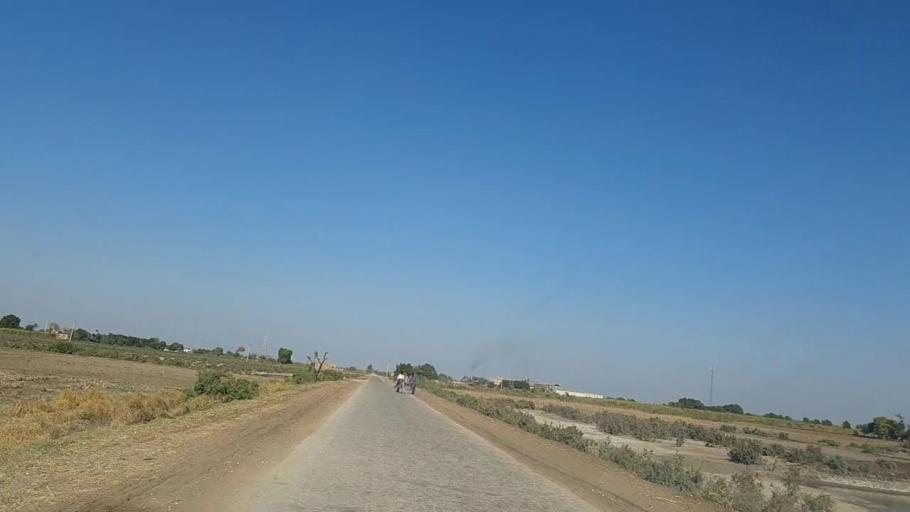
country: PK
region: Sindh
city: Digri
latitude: 25.1548
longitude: 69.0245
